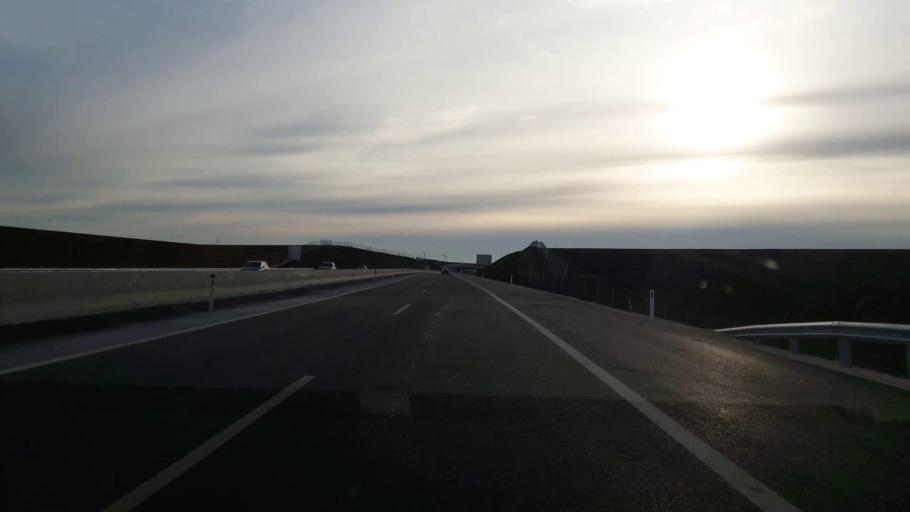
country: AT
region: Lower Austria
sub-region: Politischer Bezirk Mistelbach
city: Wilfersdorf
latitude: 48.5910
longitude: 16.6292
